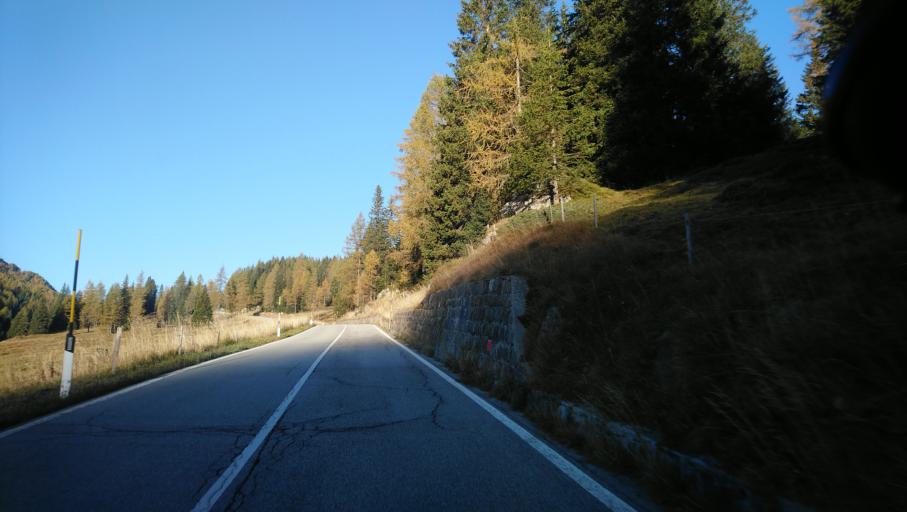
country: IT
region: Veneto
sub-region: Provincia di Belluno
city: Falcade Alto
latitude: 46.3786
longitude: 11.8184
